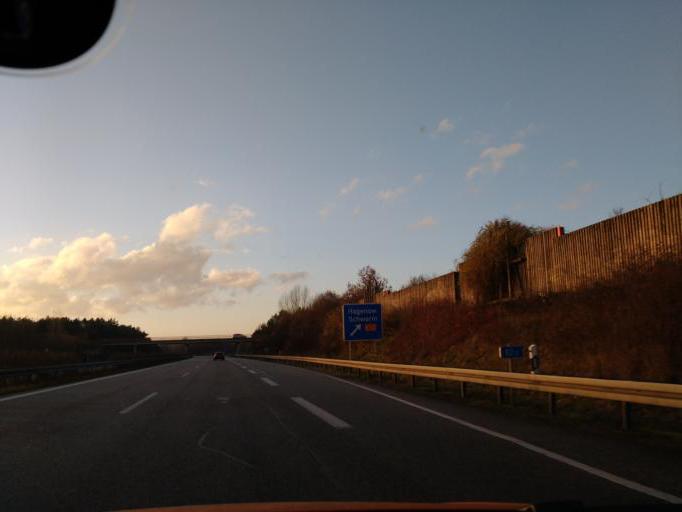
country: DE
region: Mecklenburg-Vorpommern
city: Stralendorf
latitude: 53.4855
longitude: 11.2742
